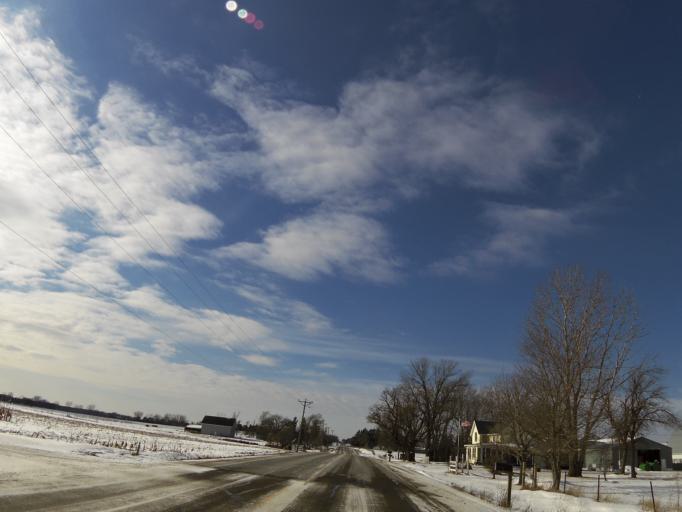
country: US
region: Wisconsin
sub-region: Saint Croix County
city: Roberts
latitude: 44.9927
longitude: -92.5667
